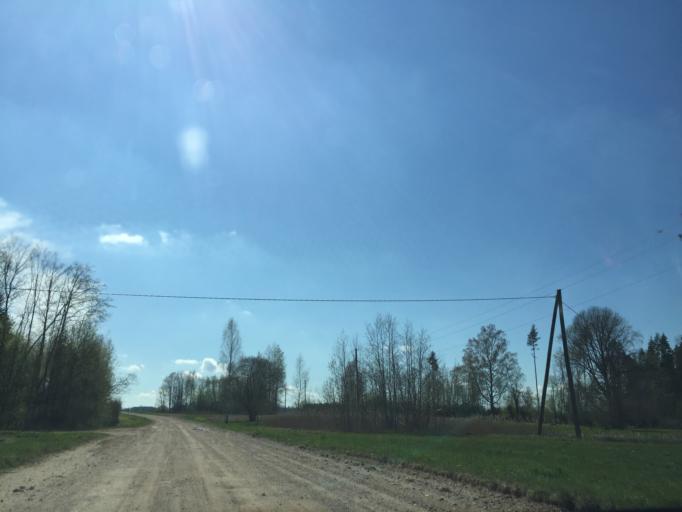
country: LV
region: Smiltene
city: Smiltene
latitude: 57.5519
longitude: 25.8531
